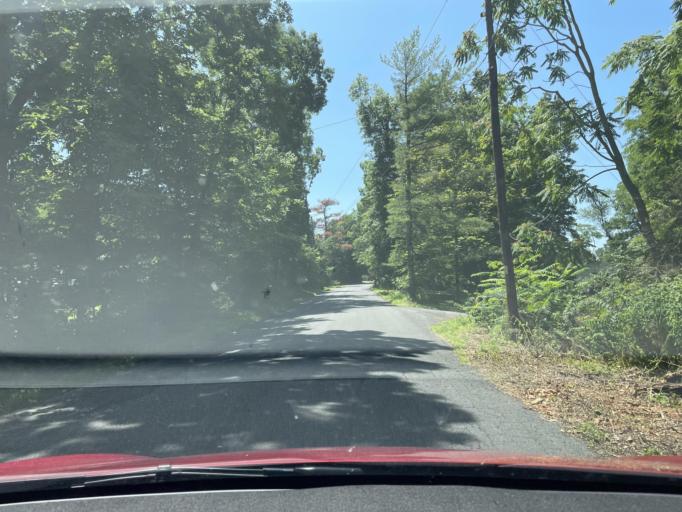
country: US
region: New York
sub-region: Ulster County
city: Lake Katrine
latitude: 42.0166
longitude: -73.9763
